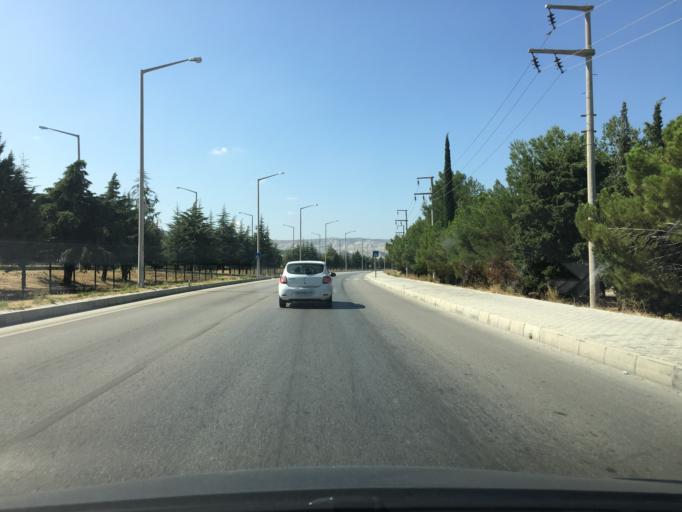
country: TR
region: Burdur
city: Burdur
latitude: 37.7331
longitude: 30.3091
